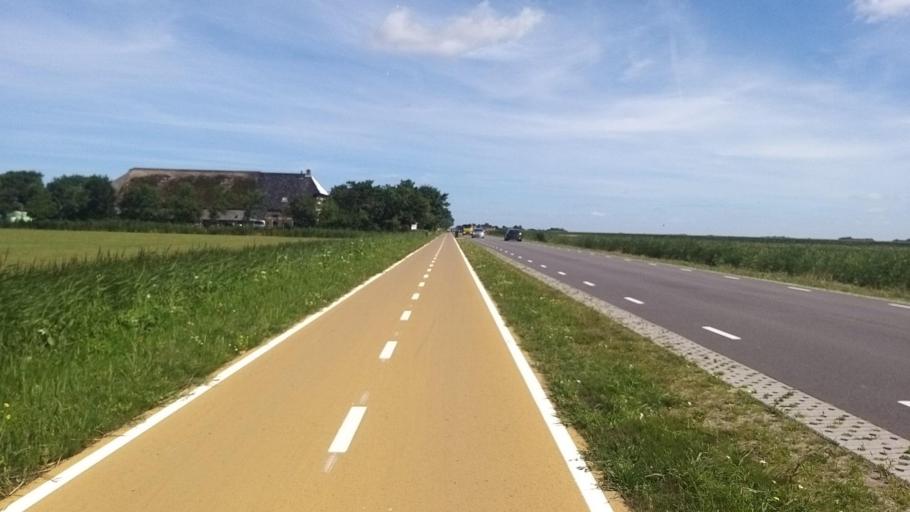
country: NL
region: North Holland
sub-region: Gemeente Texel
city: Den Burg
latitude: 53.1023
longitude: 4.8081
